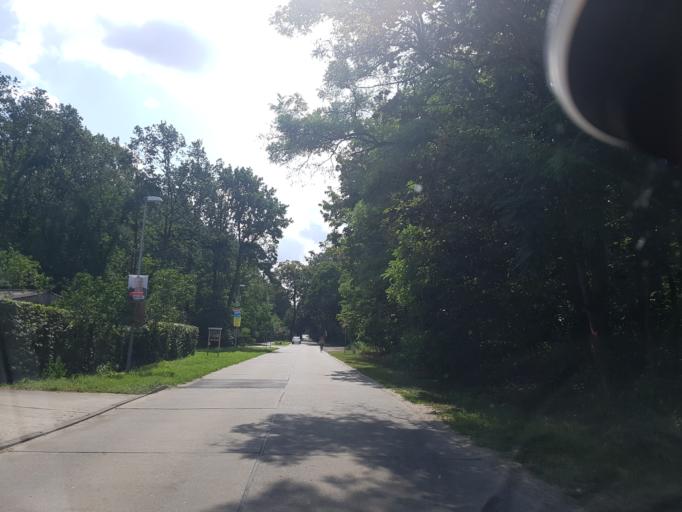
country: DE
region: Brandenburg
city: Gross Kreutz
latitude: 52.3342
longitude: 12.7274
